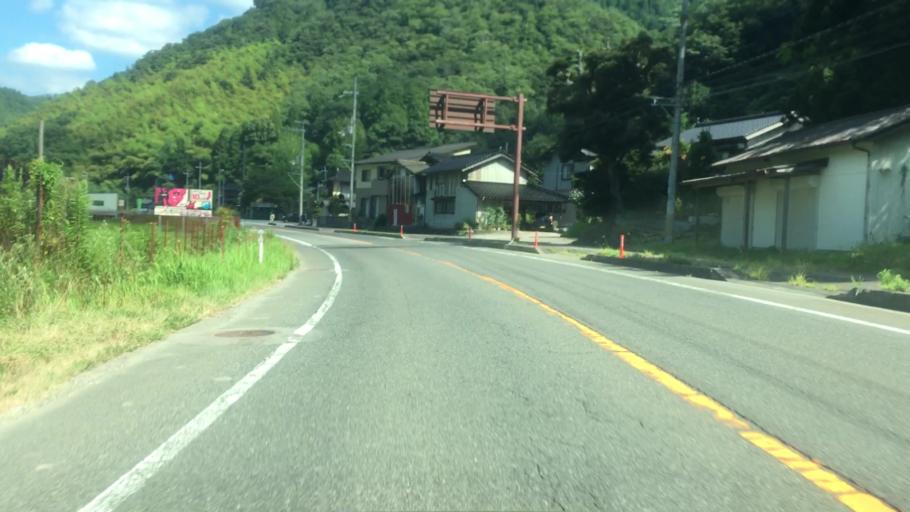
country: JP
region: Hyogo
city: Toyooka
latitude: 35.5698
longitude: 134.7811
